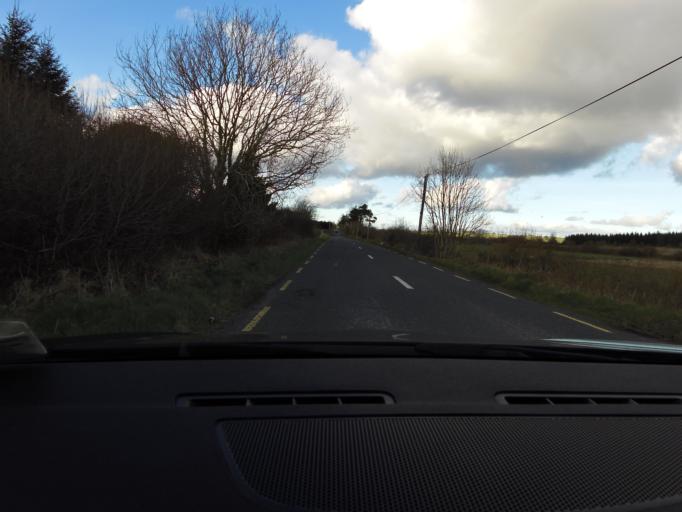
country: IE
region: Connaught
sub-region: Roscommon
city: Castlerea
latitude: 53.6645
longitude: -8.5042
